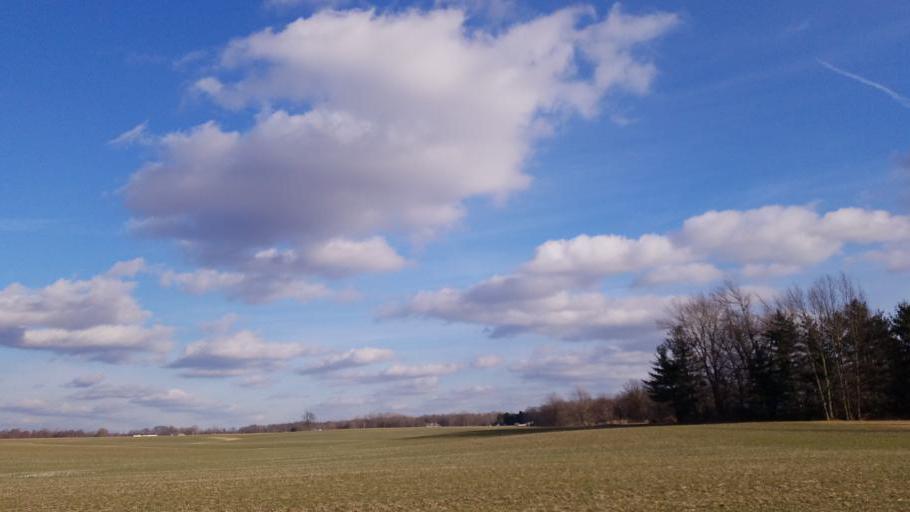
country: US
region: Ohio
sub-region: Morrow County
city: Mount Gilead
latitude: 40.5897
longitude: -82.7289
